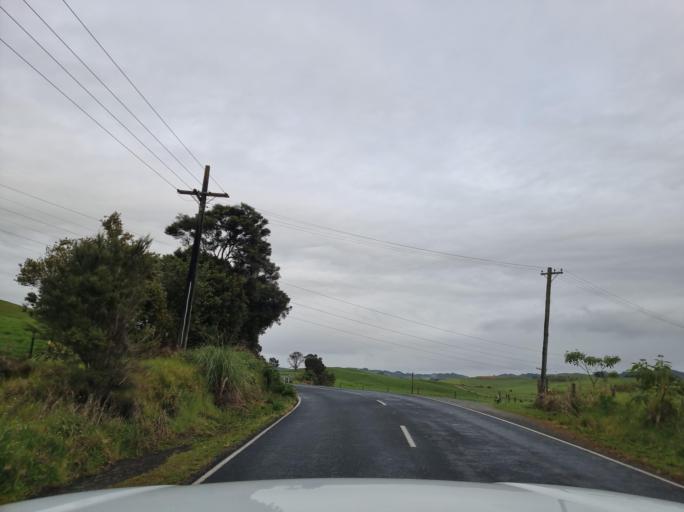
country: NZ
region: Northland
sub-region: Whangarei
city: Ruakaka
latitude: -35.9702
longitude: 174.4278
